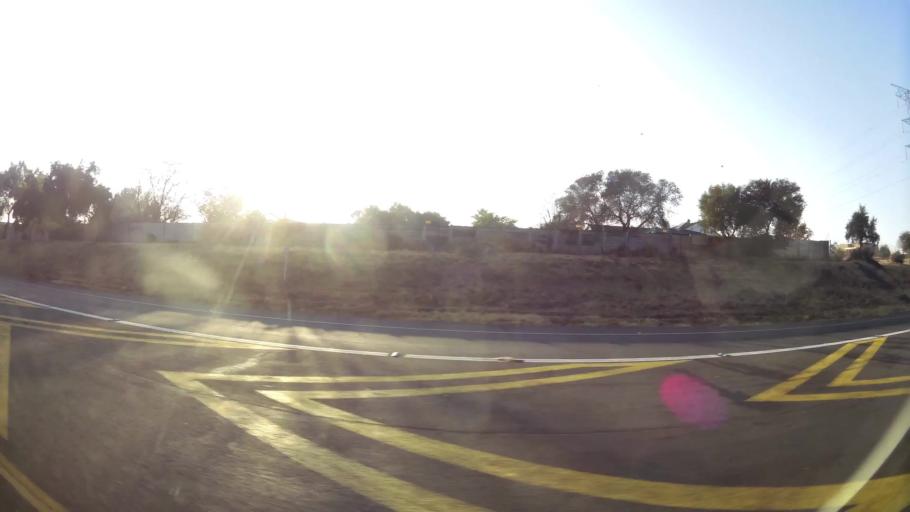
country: ZA
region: Orange Free State
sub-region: Mangaung Metropolitan Municipality
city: Bloemfontein
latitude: -29.1241
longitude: 26.1630
